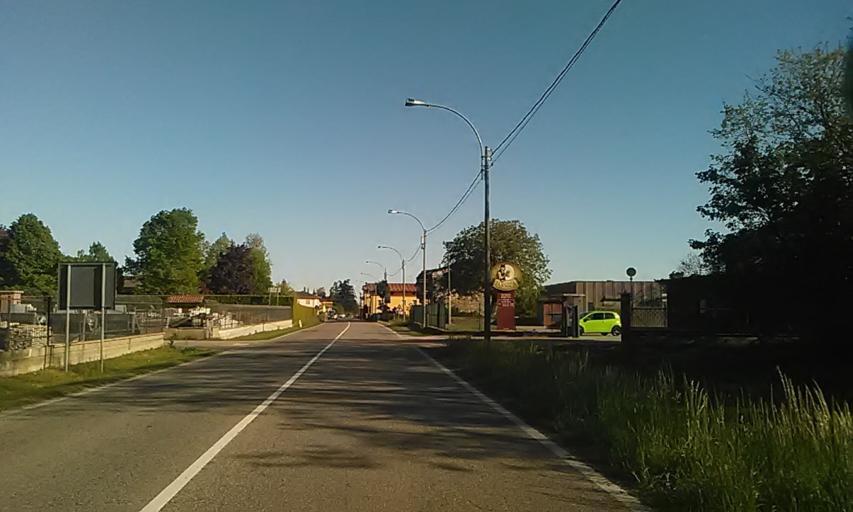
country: IT
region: Piedmont
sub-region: Provincia di Novara
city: Cavaglietto
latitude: 45.6173
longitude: 8.5167
